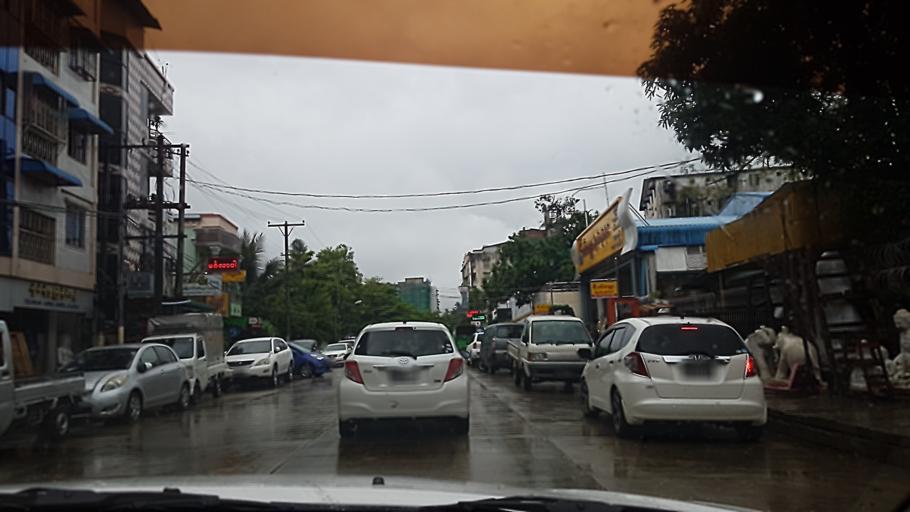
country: MM
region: Yangon
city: Yangon
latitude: 16.8032
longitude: 96.1542
